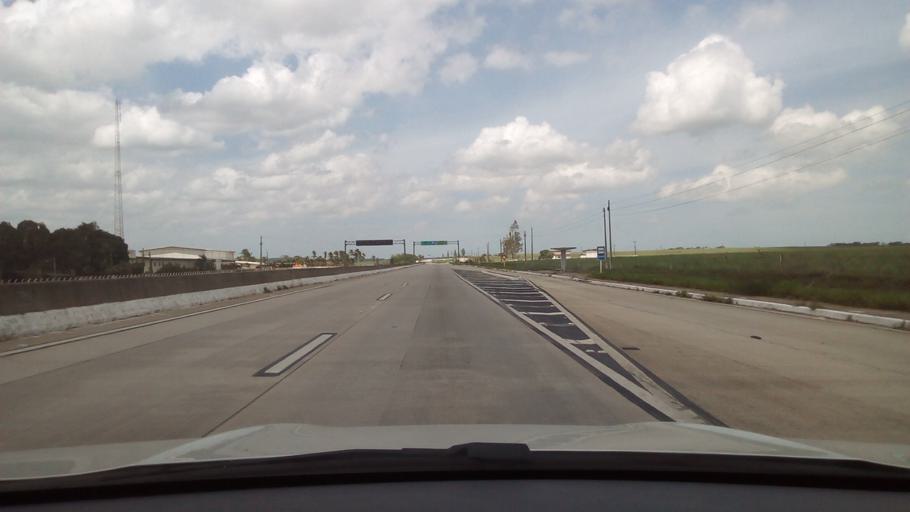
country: BR
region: Paraiba
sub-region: Mamanguape
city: Mamanguape
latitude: -6.7978
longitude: -35.1381
